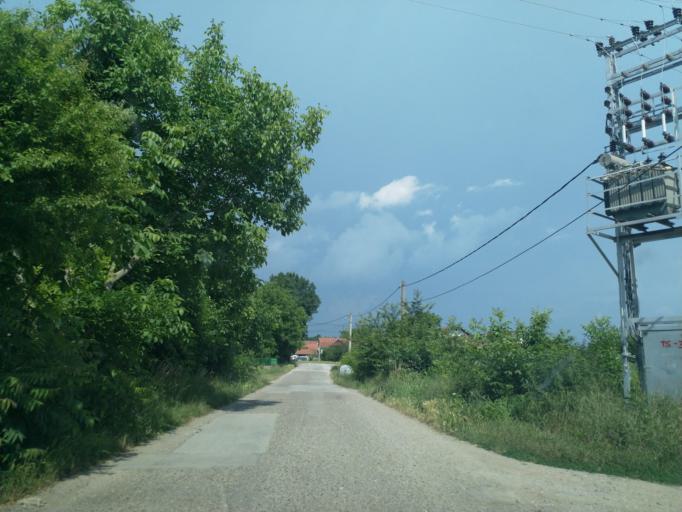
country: RS
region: Central Serbia
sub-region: Pomoravski Okrug
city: Cuprija
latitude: 43.9548
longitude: 21.3244
